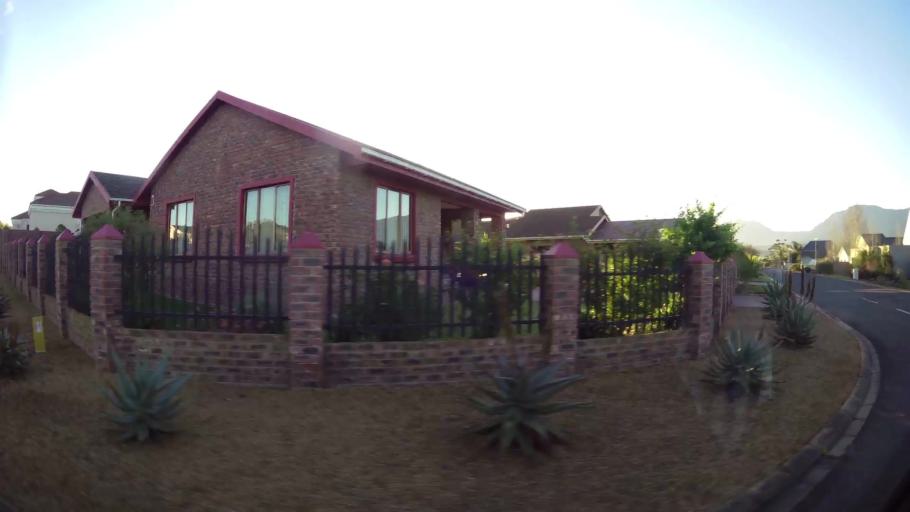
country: ZA
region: Western Cape
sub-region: Eden District Municipality
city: Riversdale
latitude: -34.0827
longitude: 21.2438
